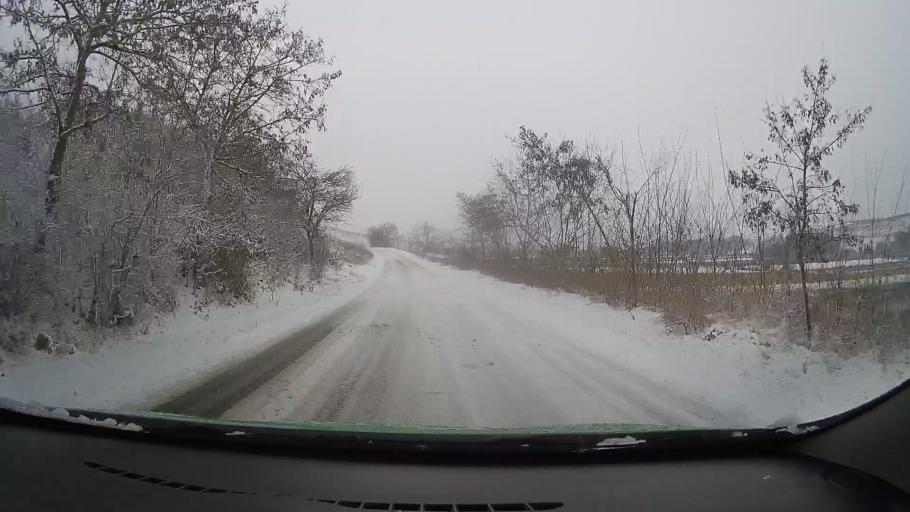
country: RO
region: Hunedoara
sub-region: Comuna Pestisu Mic
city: Pestisu Mic
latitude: 45.7985
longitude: 22.8906
